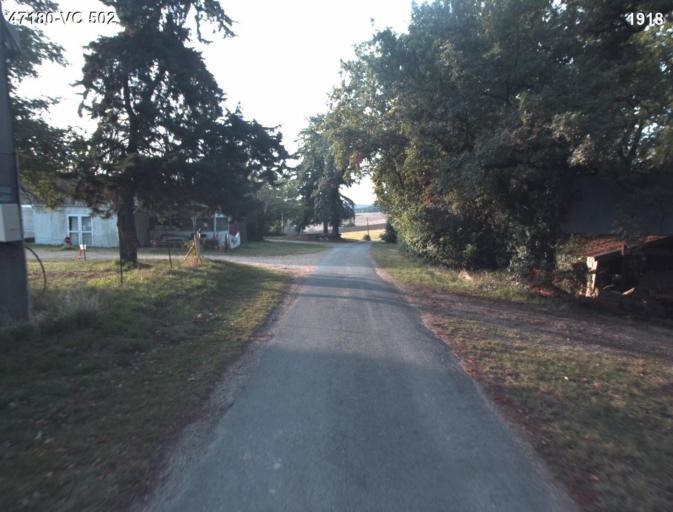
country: FR
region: Aquitaine
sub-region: Departement du Lot-et-Garonne
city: Sainte-Colombe-en-Bruilhois
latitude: 44.1739
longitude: 0.4826
